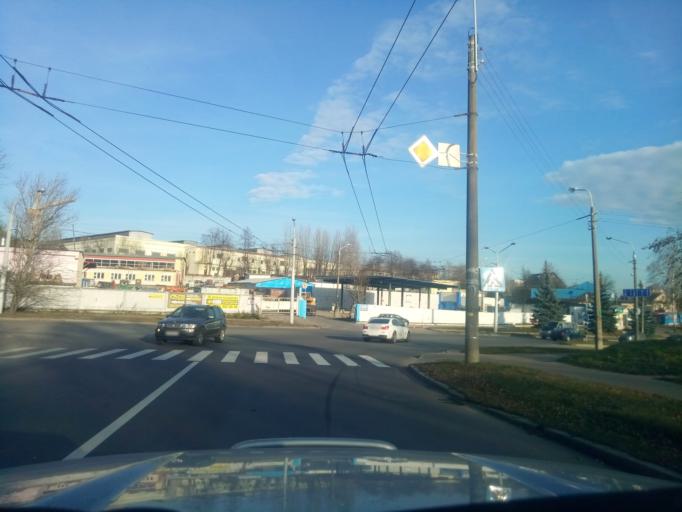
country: BY
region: Minsk
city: Novoye Medvezhino
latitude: 53.8856
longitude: 27.4983
